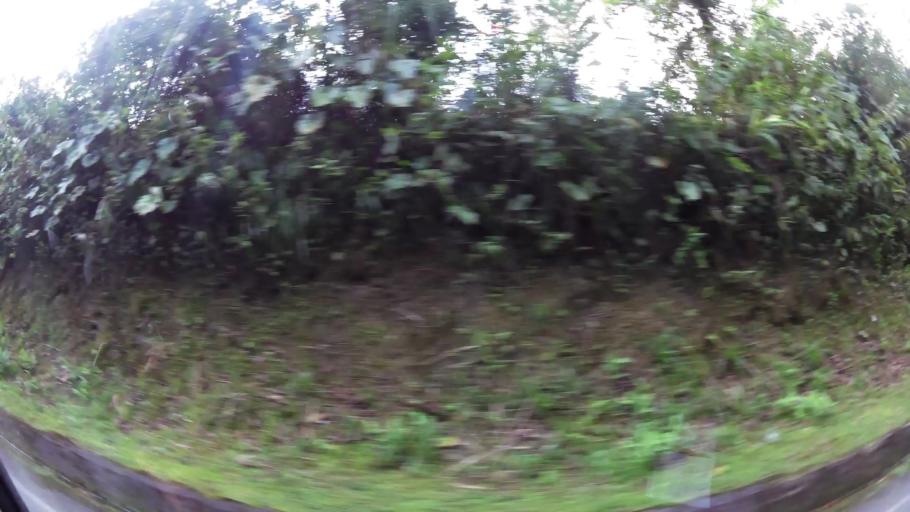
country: EC
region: Pastaza
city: Puyo
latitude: -1.4359
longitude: -78.1783
